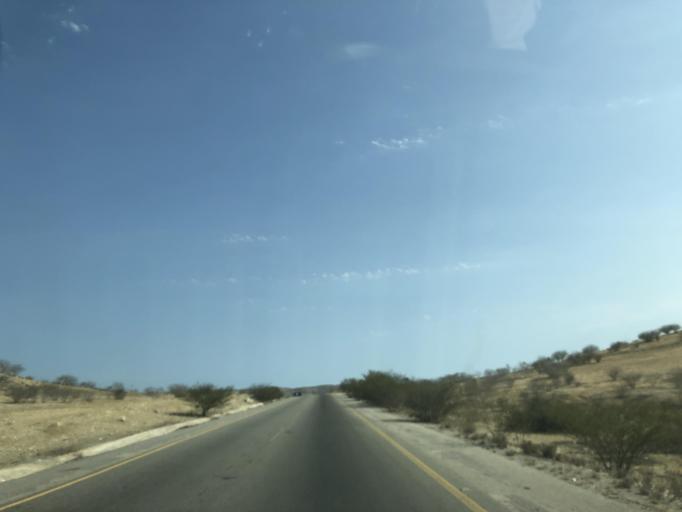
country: AO
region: Benguela
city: Benguela
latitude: -12.7342
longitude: 13.3491
